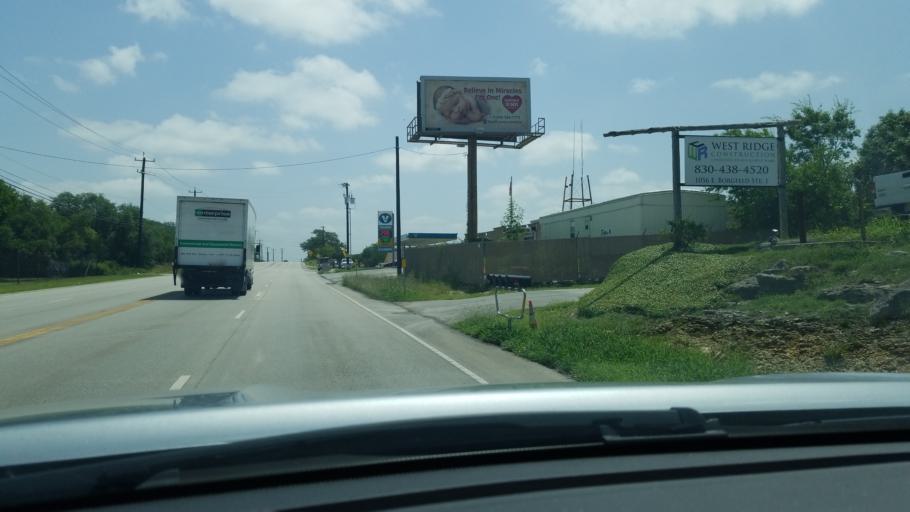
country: US
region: Texas
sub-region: Bexar County
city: Timberwood Park
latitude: 29.7133
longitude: -98.4769
